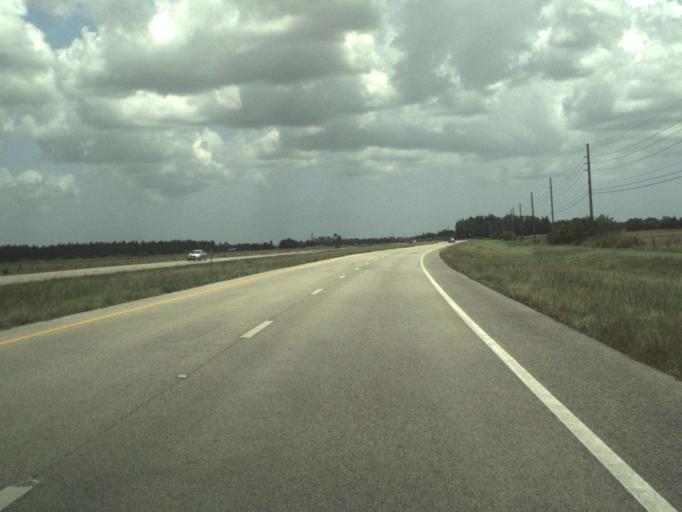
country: US
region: Florida
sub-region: Saint Lucie County
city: Fort Pierce South
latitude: 27.3833
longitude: -80.4690
